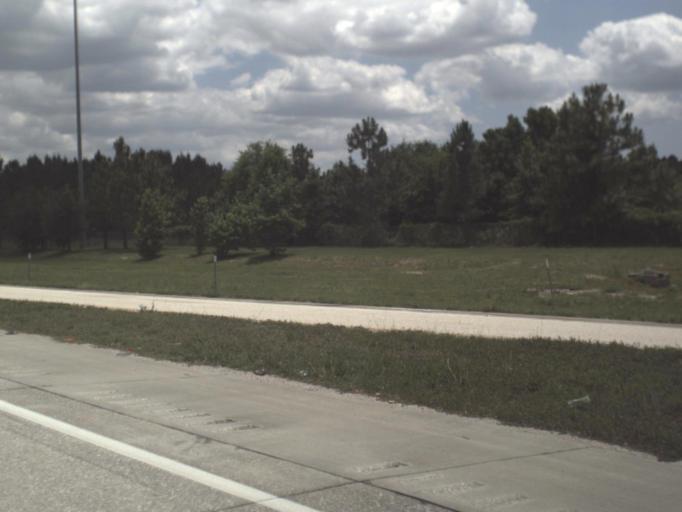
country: US
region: Florida
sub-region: Saint Johns County
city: Ponte Vedra Beach
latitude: 30.2479
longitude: -81.5153
